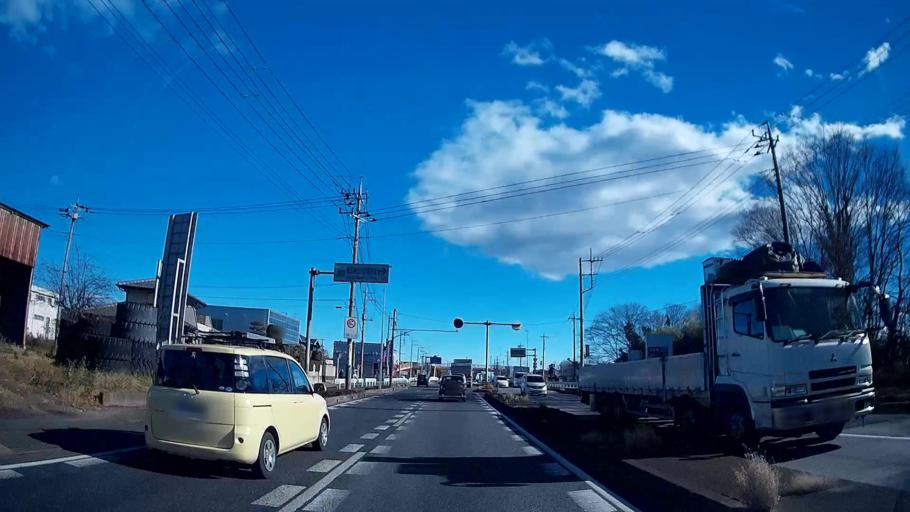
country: JP
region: Saitama
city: Yorii
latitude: 36.1219
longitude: 139.2097
